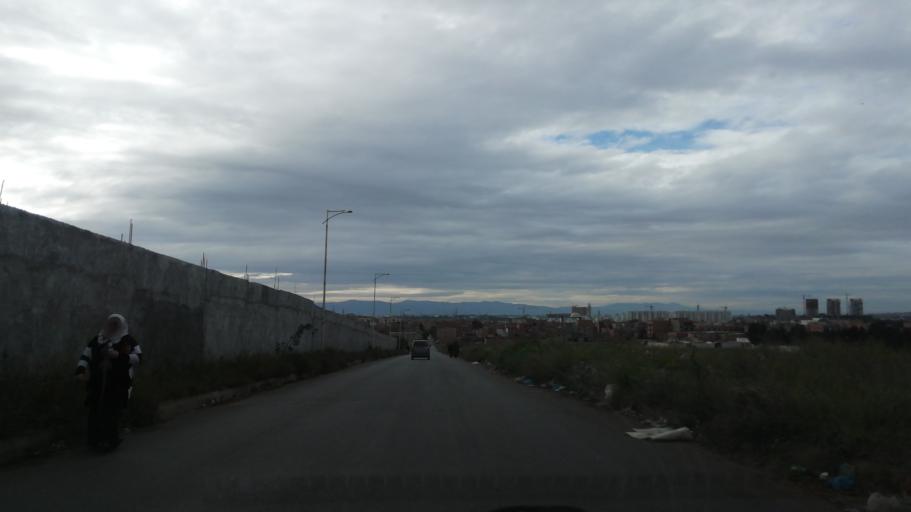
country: DZ
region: Oran
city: Oran
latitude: 35.6916
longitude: -0.5967
